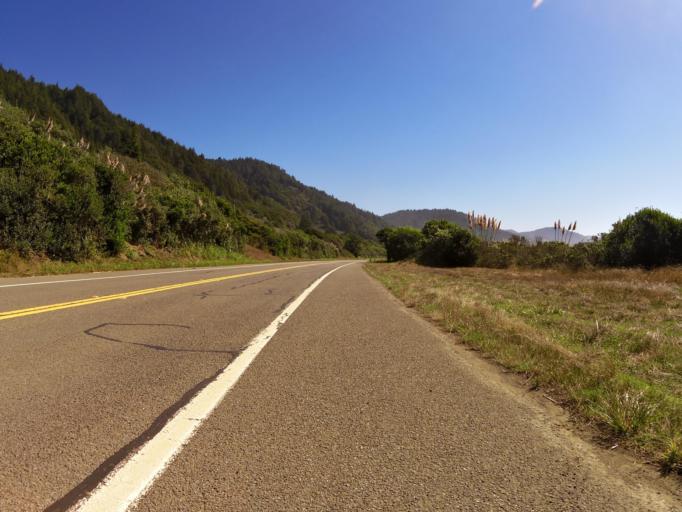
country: US
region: California
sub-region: Mendocino County
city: Fort Bragg
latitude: 39.6917
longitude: -123.7949
